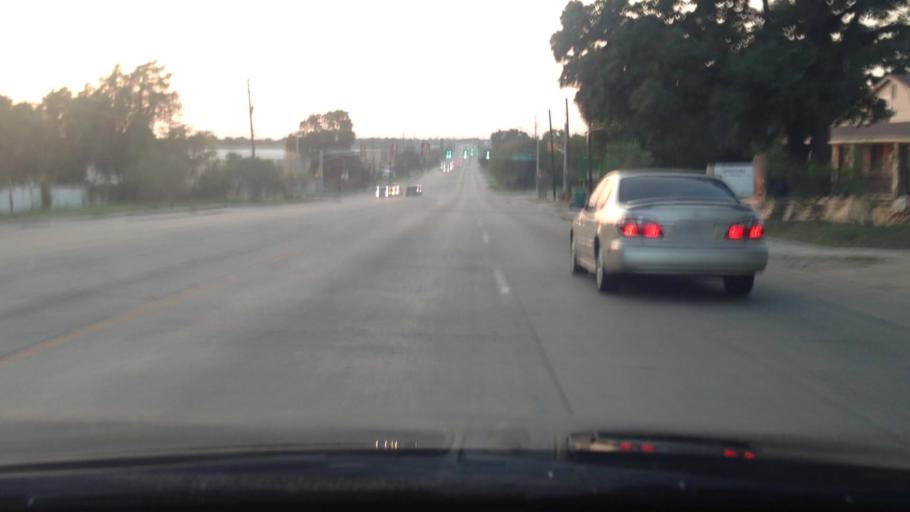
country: US
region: Texas
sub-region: Tarrant County
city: Kennedale
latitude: 32.6540
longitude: -97.2291
